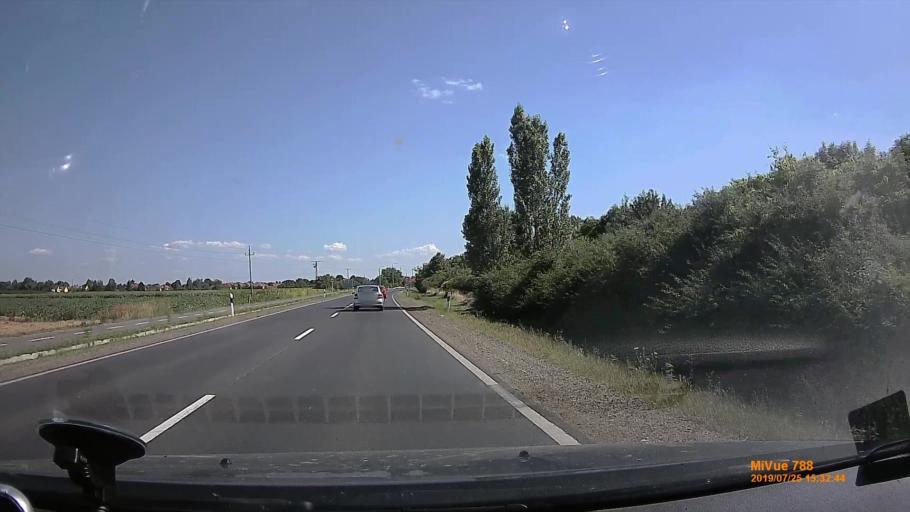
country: HU
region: Borsod-Abauj-Zemplen
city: Malyi
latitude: 48.0032
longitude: 20.8303
